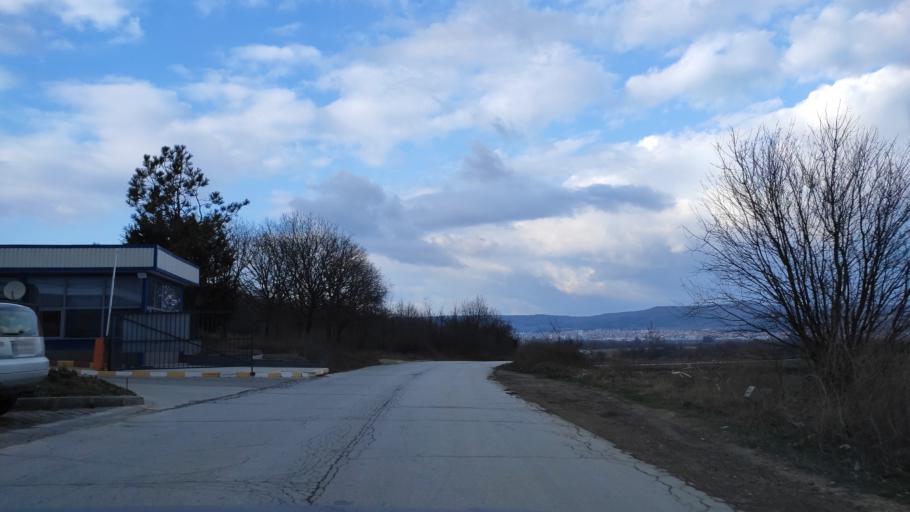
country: BG
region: Varna
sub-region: Obshtina Aksakovo
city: Aksakovo
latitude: 43.2264
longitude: 27.8049
